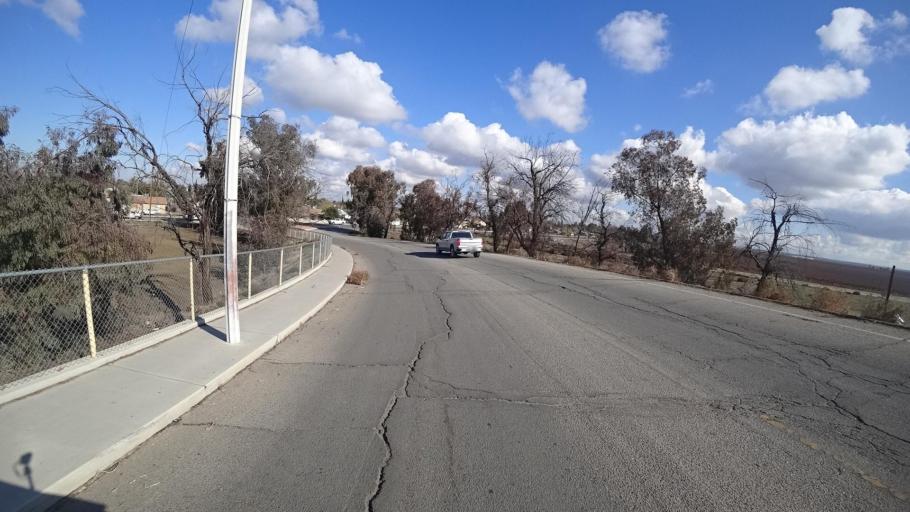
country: US
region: California
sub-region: Kern County
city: McFarland
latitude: 35.6736
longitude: -119.2245
